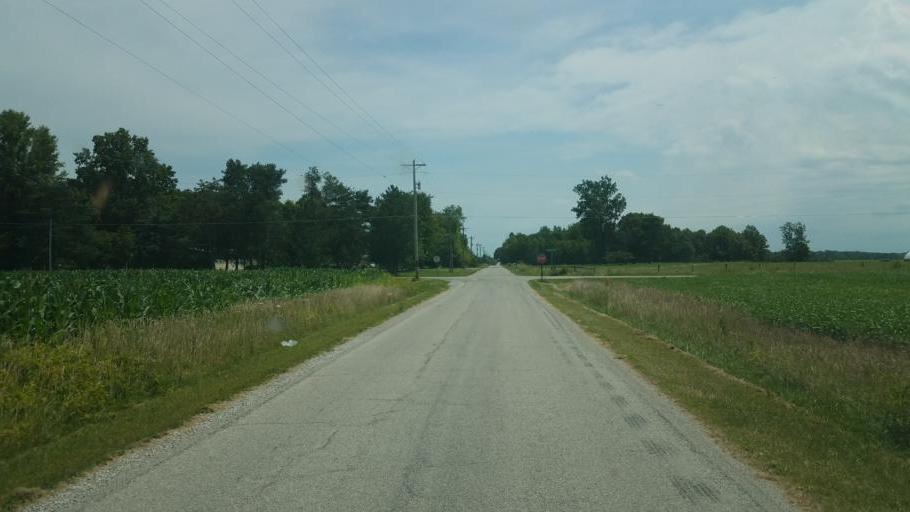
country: US
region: Ohio
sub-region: Crawford County
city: Bucyrus
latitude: 40.8775
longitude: -83.0177
